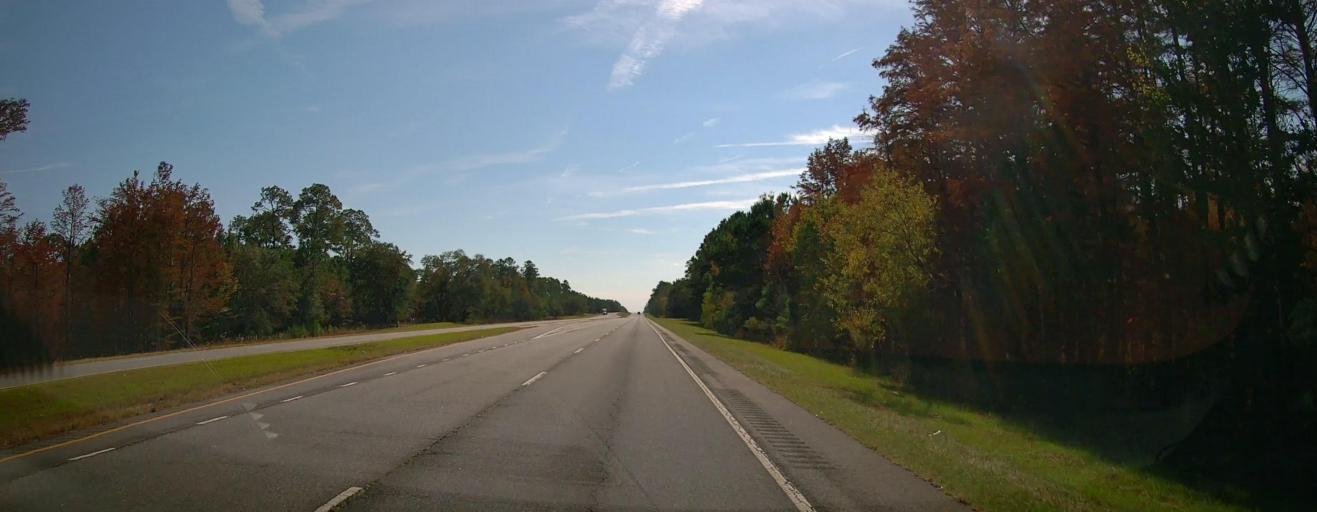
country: US
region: Georgia
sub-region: Lee County
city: Leesburg
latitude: 31.7017
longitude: -83.9913
